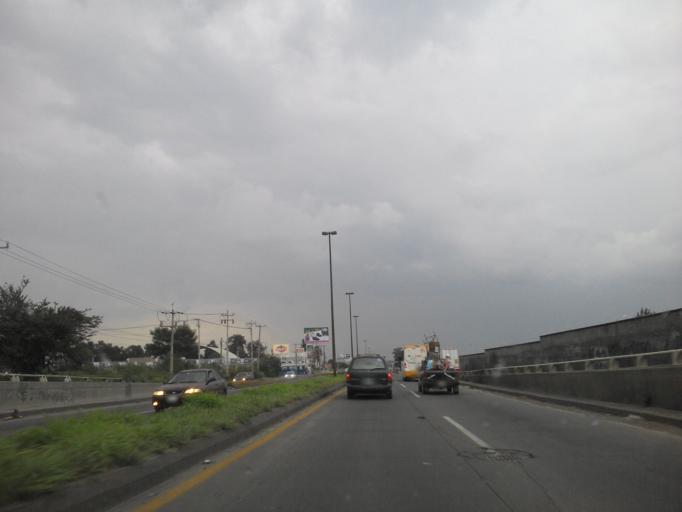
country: MX
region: Jalisco
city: Tlaquepaque
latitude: 20.6180
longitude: -103.2864
